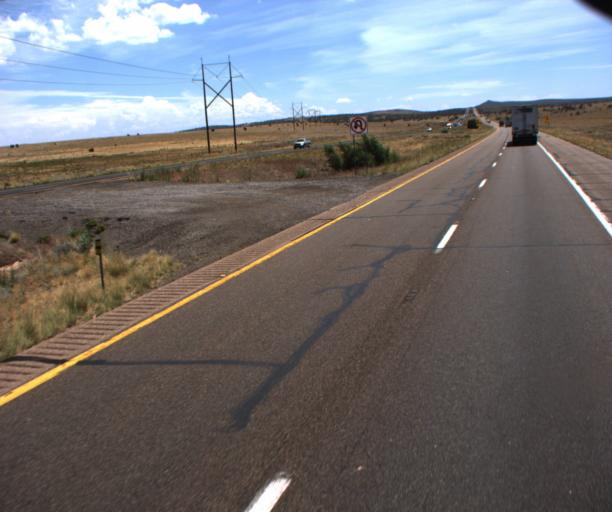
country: US
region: Arizona
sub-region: Yavapai County
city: Paulden
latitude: 35.2898
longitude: -112.8177
